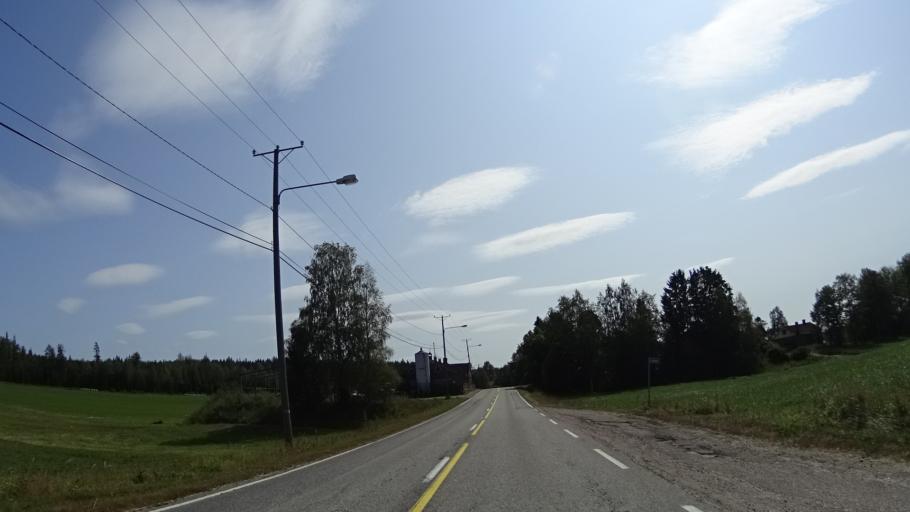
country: FI
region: Pirkanmaa
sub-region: Ylae-Pirkanmaa
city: Maenttae
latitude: 61.9109
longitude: 24.7816
